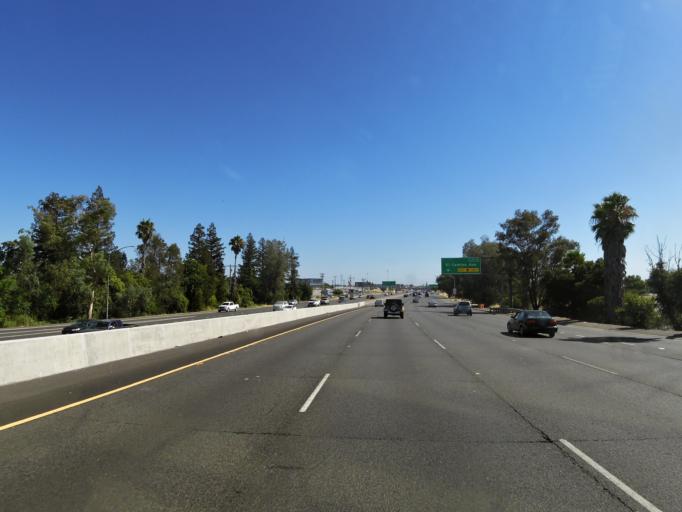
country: US
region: California
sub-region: Sacramento County
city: Arden-Arcade
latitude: 38.6057
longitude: -121.4327
